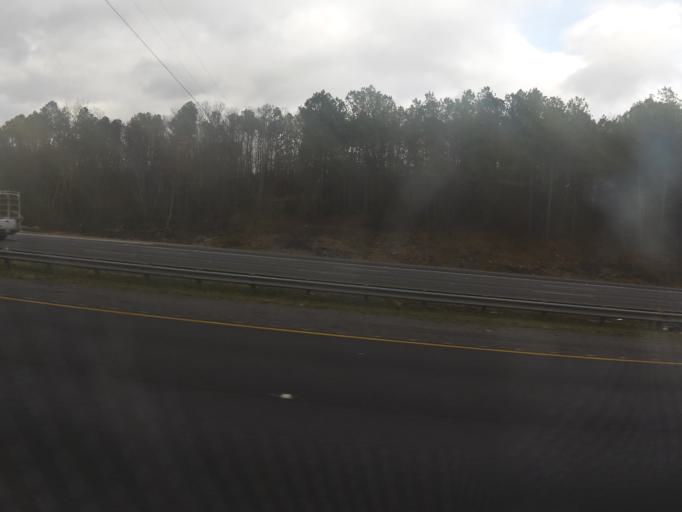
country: US
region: Georgia
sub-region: Catoosa County
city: Indian Springs
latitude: 34.9657
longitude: -85.1885
